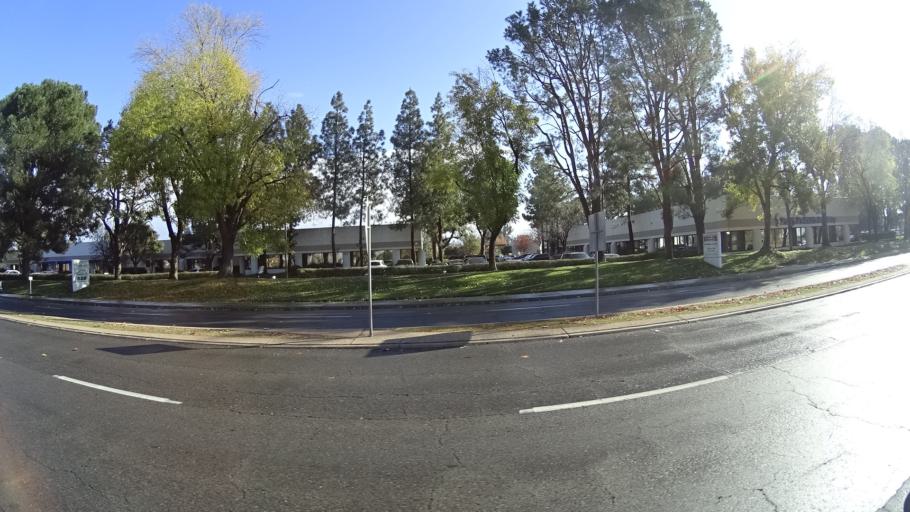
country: US
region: California
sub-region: Kern County
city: Bakersfield
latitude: 35.3668
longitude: -119.0630
